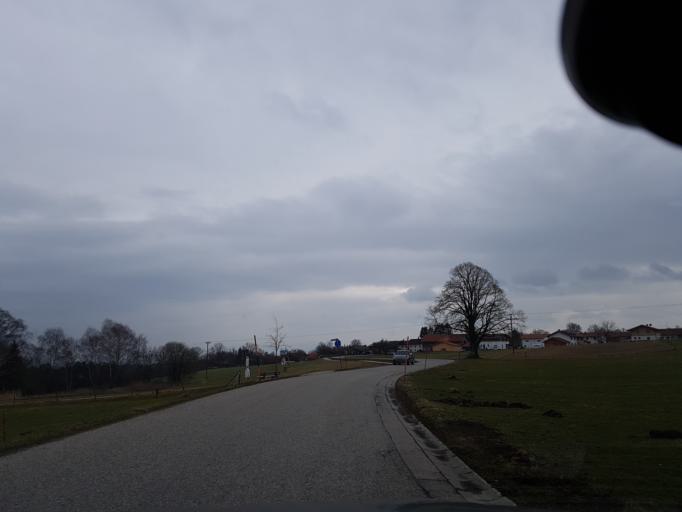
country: DE
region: Bavaria
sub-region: Upper Bavaria
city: Bruckmuhl
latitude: 47.9234
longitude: 11.9007
